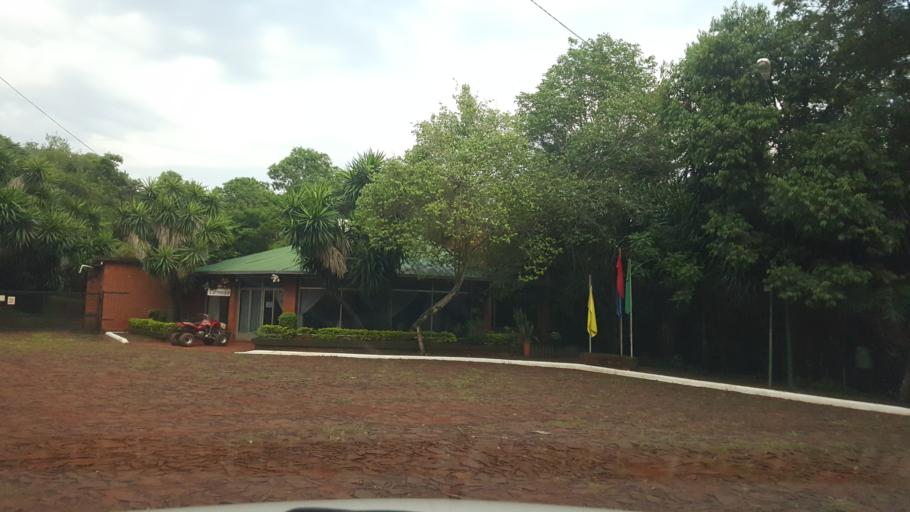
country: AR
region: Misiones
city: Capiovi
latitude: -26.9248
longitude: -55.0614
